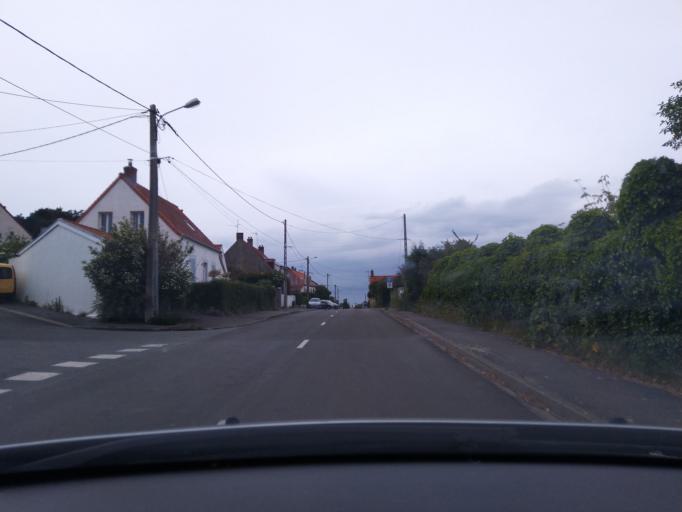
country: FR
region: Nord-Pas-de-Calais
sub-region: Departement du Pas-de-Calais
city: Wissant
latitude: 50.8825
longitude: 1.6659
